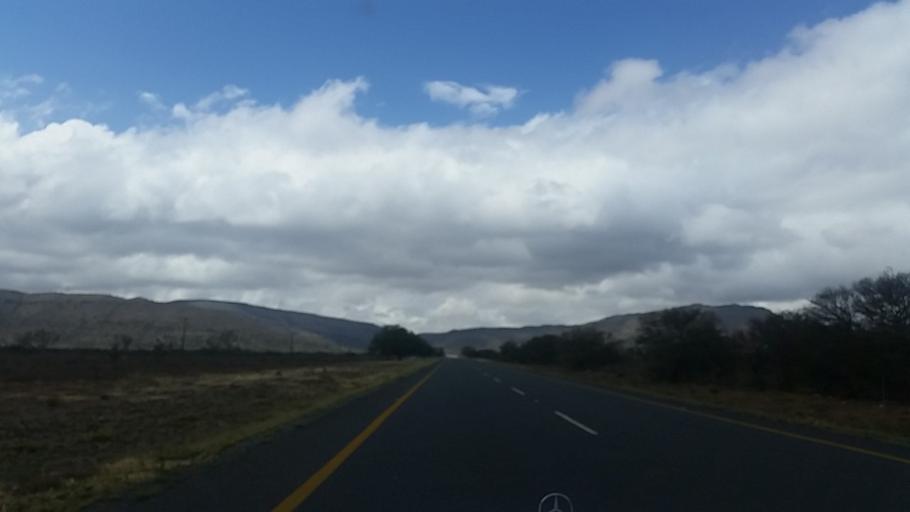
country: ZA
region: Eastern Cape
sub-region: Cacadu District Municipality
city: Graaff-Reinet
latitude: -31.9901
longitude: 24.6846
